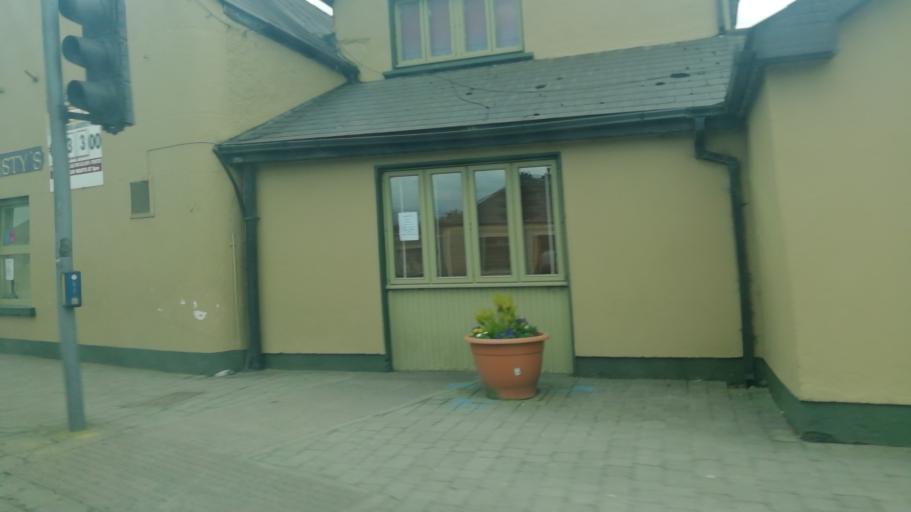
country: IE
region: Leinster
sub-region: Kildare
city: Prosperous
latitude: 53.2882
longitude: -6.7521
